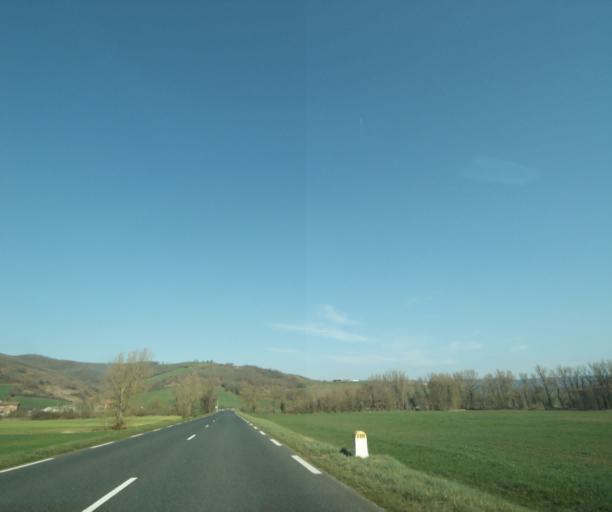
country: FR
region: Midi-Pyrenees
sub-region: Departement de l'Aveyron
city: Saint-Affrique
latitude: 43.9220
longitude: 2.8232
